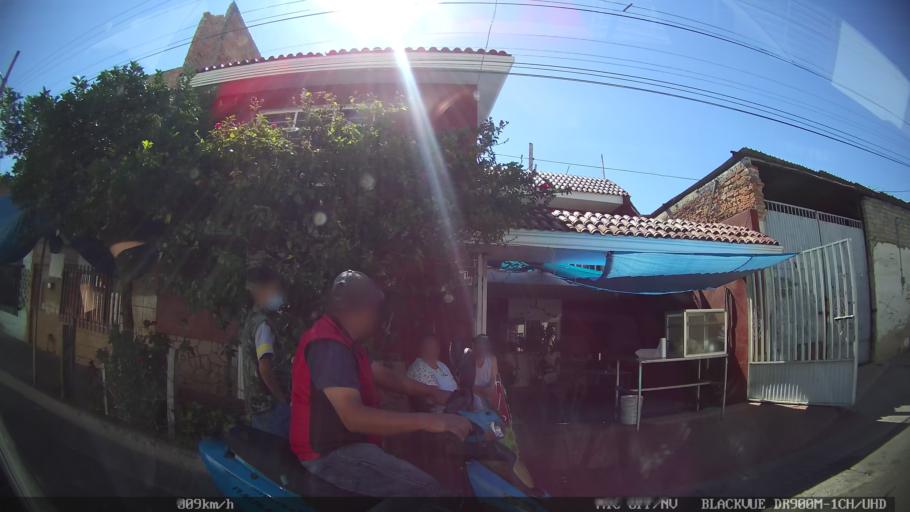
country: MX
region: Jalisco
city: Tlaquepaque
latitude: 20.6991
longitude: -103.2796
